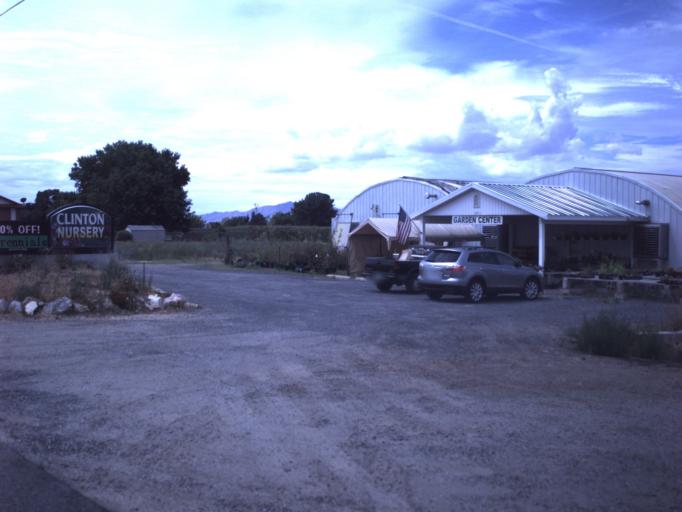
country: US
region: Utah
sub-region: Davis County
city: Clinton
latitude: 41.1295
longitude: -112.0645
